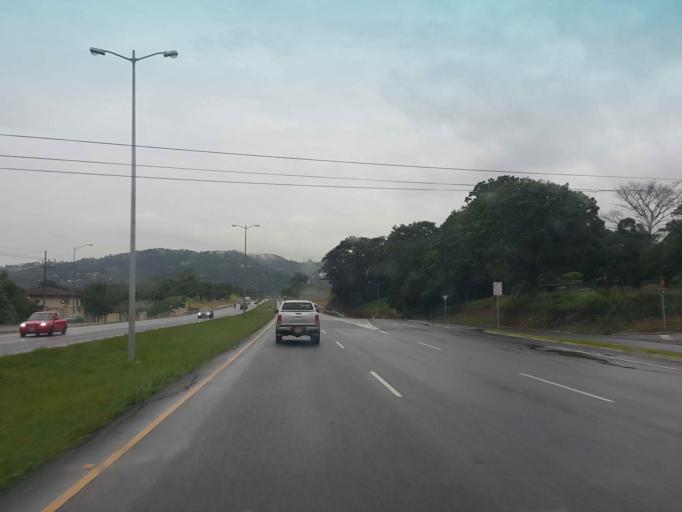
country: CR
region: San Jose
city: Santa Ana
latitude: 9.9397
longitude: -84.2023
